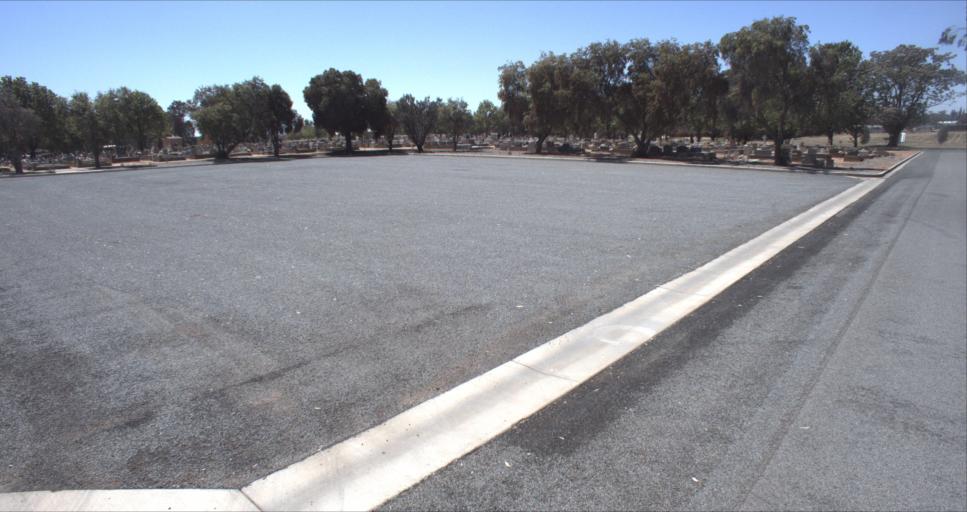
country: AU
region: New South Wales
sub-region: Leeton
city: Leeton
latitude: -34.5328
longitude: 146.3979
